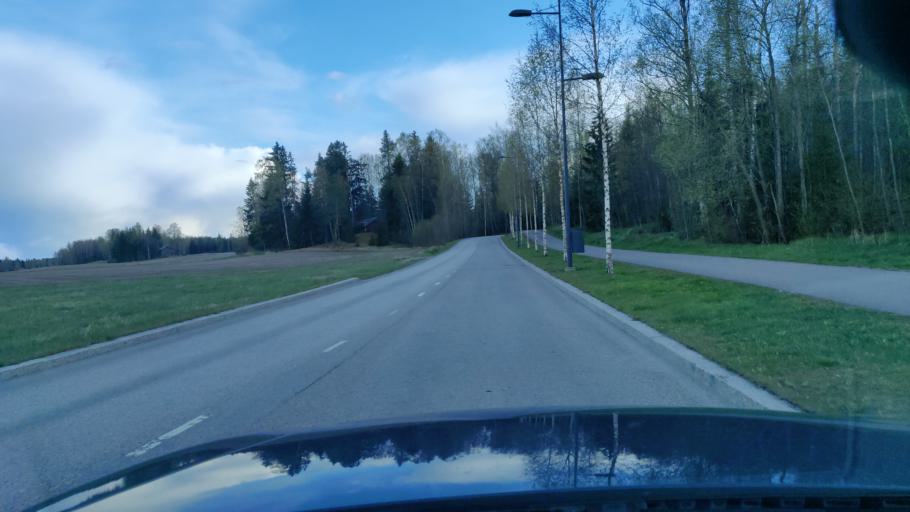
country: FI
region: Uusimaa
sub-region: Helsinki
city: Jaervenpaeae
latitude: 60.4851
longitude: 25.0573
